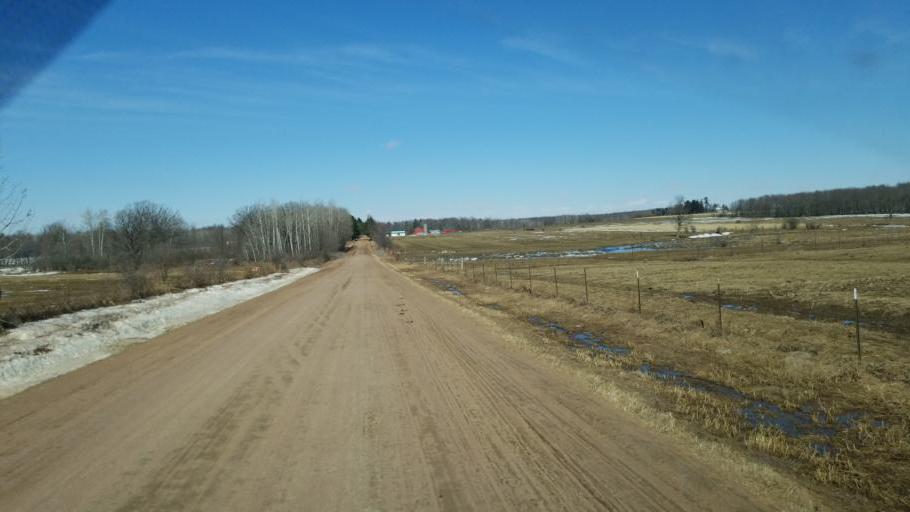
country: US
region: Wisconsin
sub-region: Marathon County
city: Spencer
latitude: 44.6015
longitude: -90.3764
